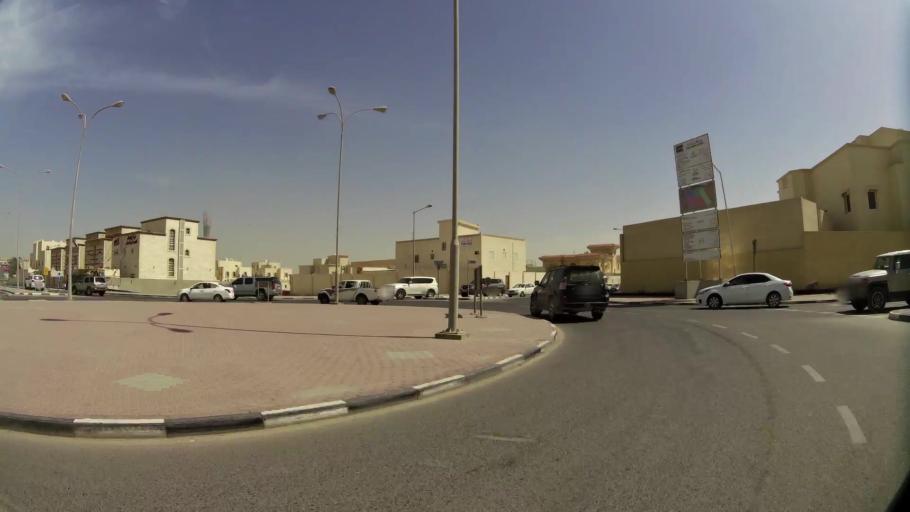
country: QA
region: Baladiyat ar Rayyan
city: Ar Rayyan
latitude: 25.2683
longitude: 51.4263
